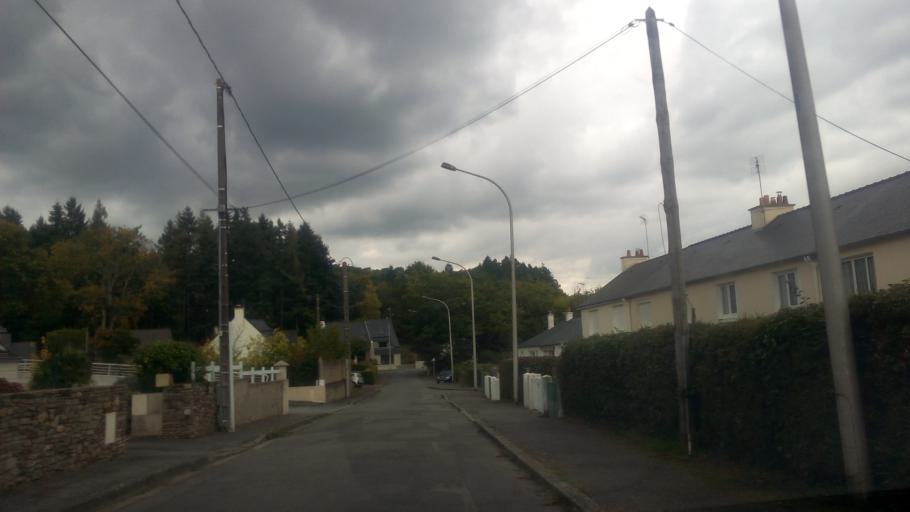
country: FR
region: Brittany
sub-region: Departement d'Ille-et-Vilaine
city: Redon
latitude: 47.6605
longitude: -2.0865
